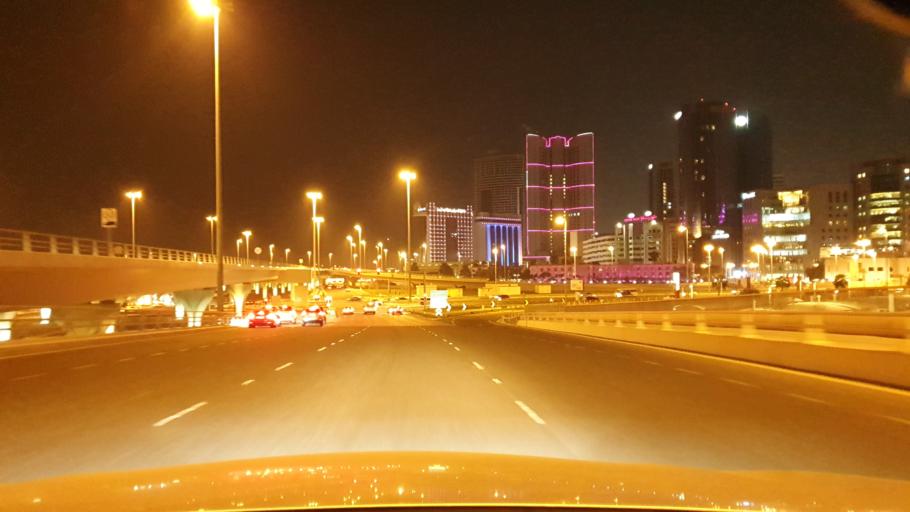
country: BH
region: Muharraq
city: Al Muharraq
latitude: 26.2475
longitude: 50.5882
